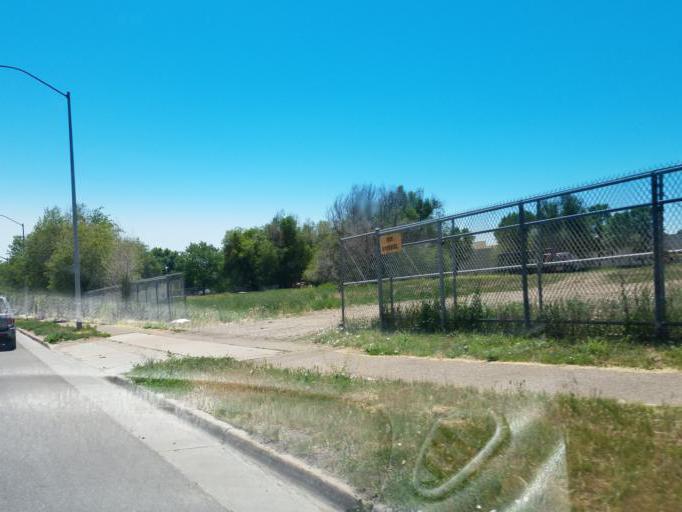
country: US
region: Colorado
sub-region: Larimer County
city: Fort Collins
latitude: 40.5793
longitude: -105.0600
